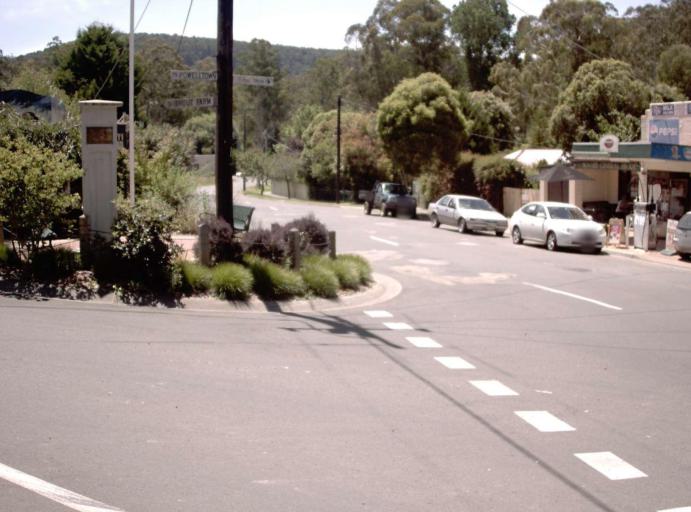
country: AU
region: Victoria
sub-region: Baw Baw
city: Warragul
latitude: -37.8937
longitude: 145.9999
